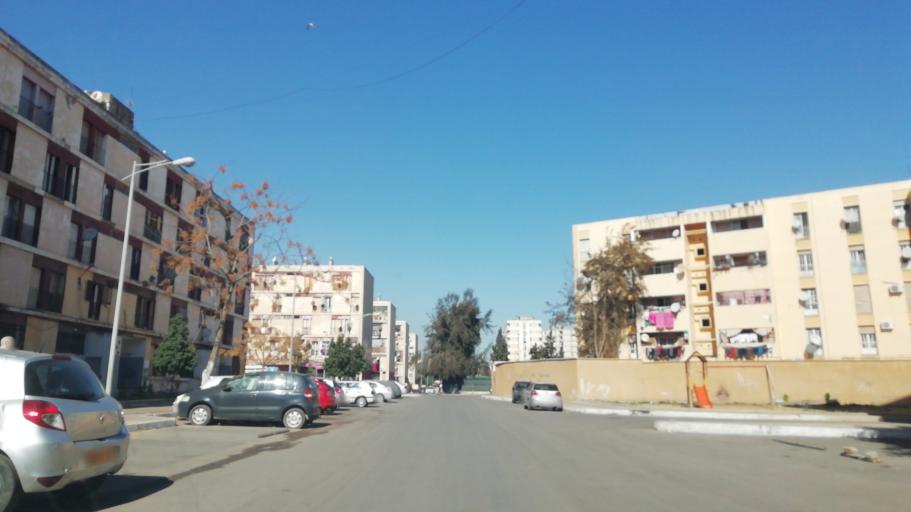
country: DZ
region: Oran
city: Oran
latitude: 35.6786
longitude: -0.6383
